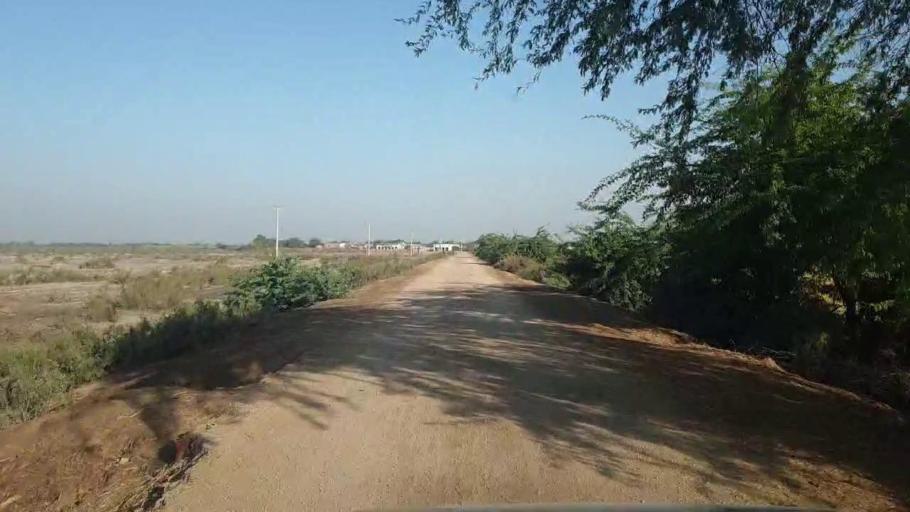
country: PK
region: Sindh
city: Badin
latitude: 24.6981
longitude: 68.8164
